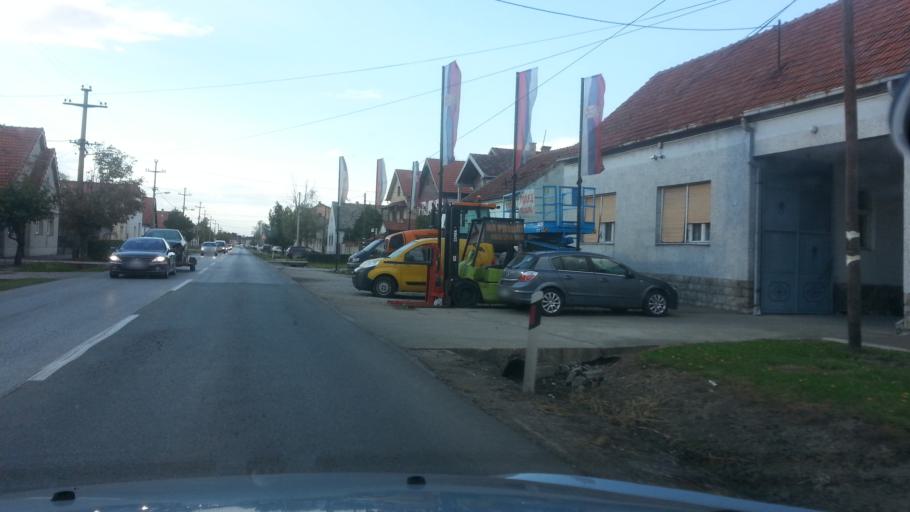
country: RS
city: Novi Banovci
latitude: 44.9097
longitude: 20.2687
